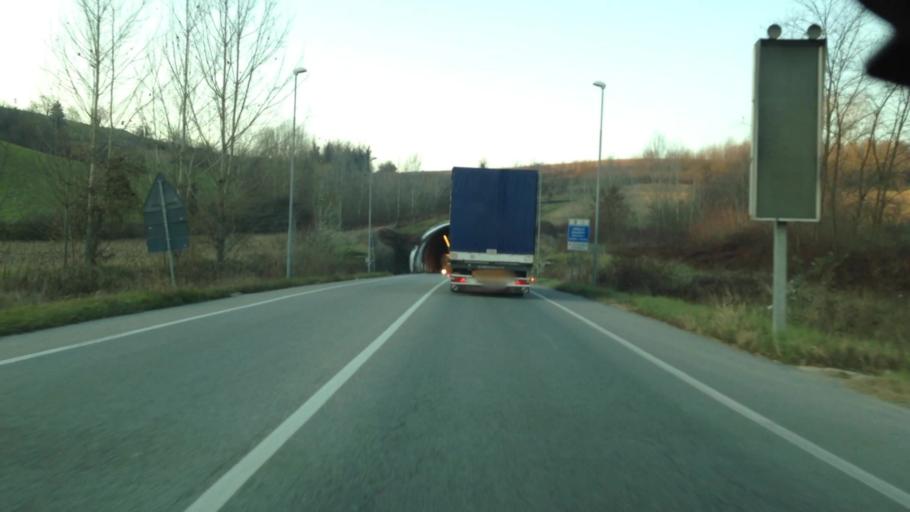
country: IT
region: Piedmont
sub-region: Provincia di Asti
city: Piano-Molini d'Isola
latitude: 44.8312
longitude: 8.2023
